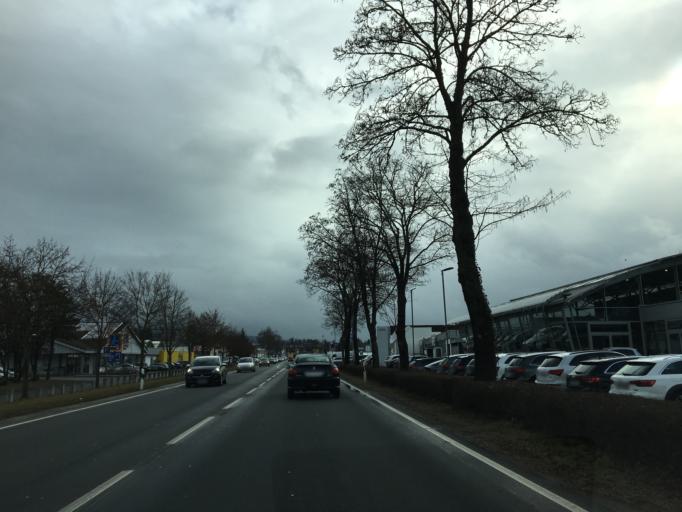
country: DE
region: Hesse
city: Michelstadt
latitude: 49.6800
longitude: 9.0001
